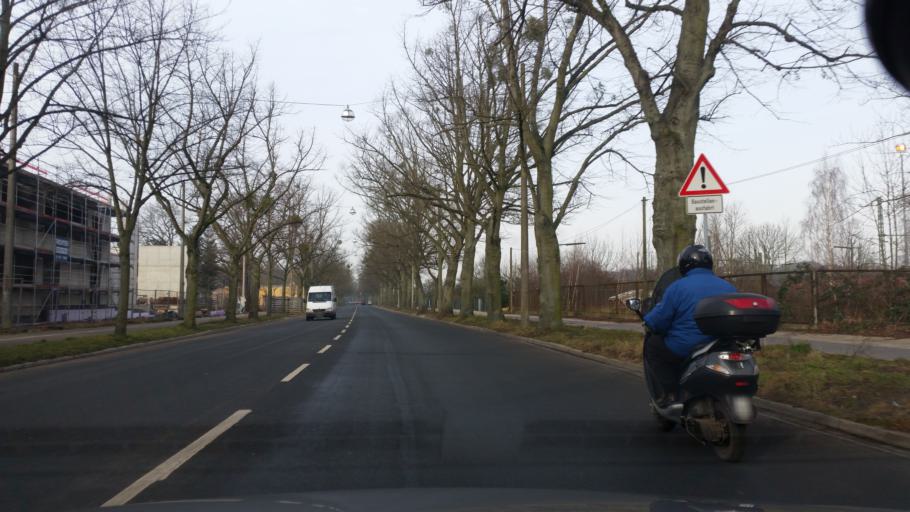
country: DE
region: Lower Saxony
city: Hannover
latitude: 52.3948
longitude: 9.7072
